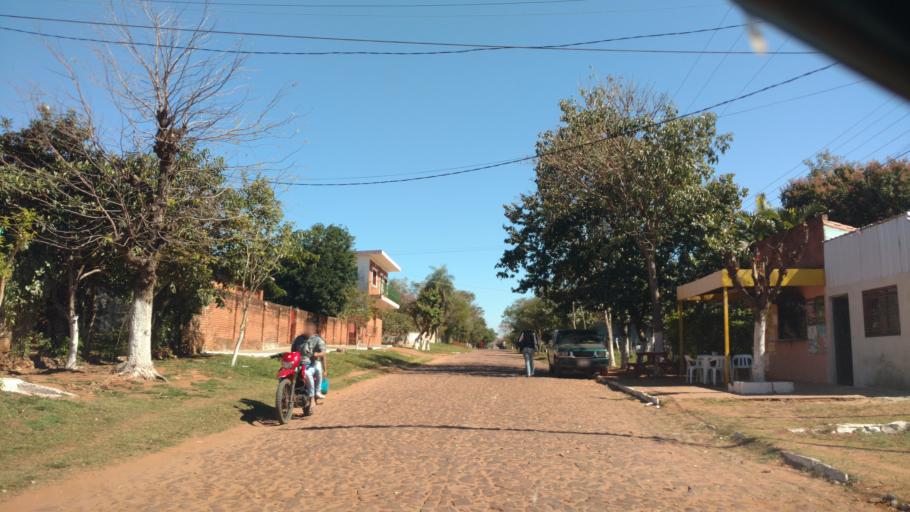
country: PY
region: Paraguari
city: Yaguaron
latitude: -25.5636
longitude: -57.2929
